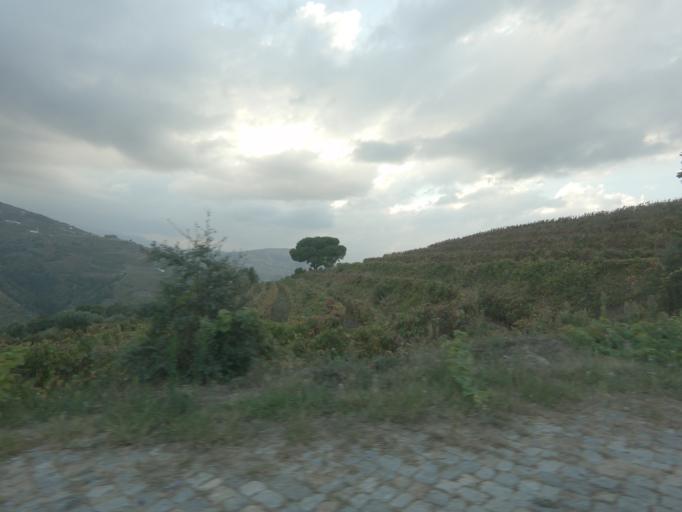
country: PT
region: Vila Real
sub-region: Mesao Frio
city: Mesao Frio
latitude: 41.1623
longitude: -7.8522
